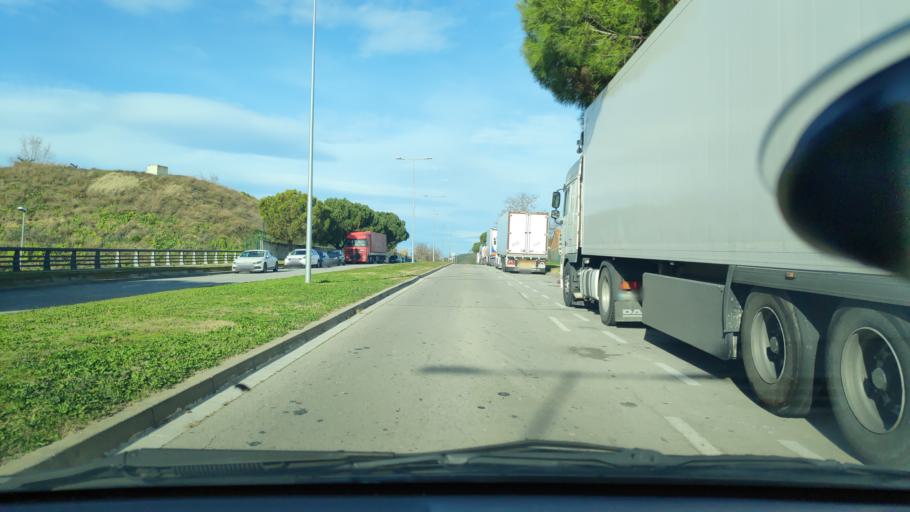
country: ES
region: Catalonia
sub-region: Provincia de Barcelona
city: Rubi
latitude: 41.4876
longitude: 2.0472
